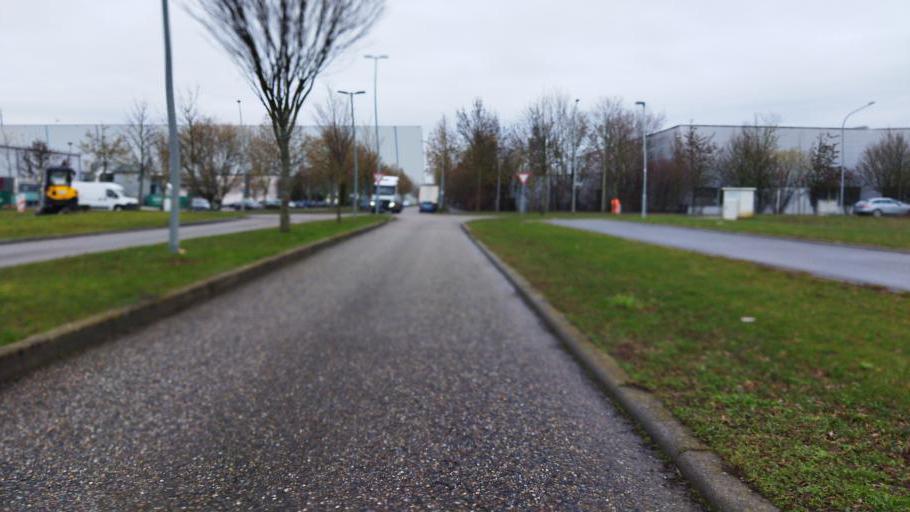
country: DE
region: Baden-Wuerttemberg
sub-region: Regierungsbezirk Stuttgart
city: Untereisesheim
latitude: 49.1820
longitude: 9.1680
